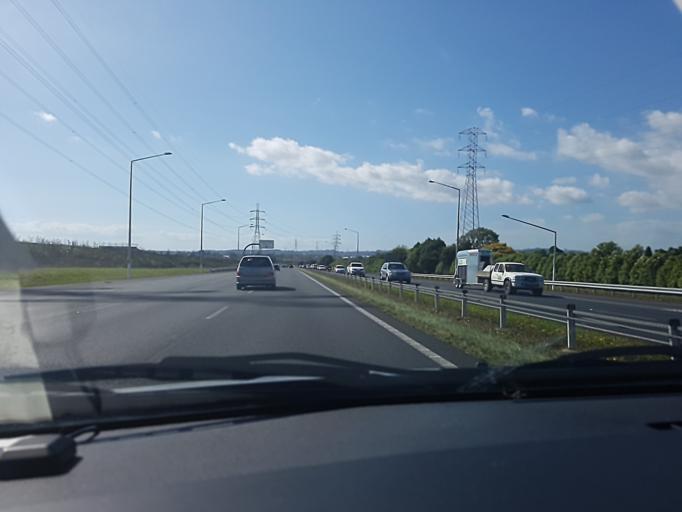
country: NZ
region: Auckland
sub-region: Auckland
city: Papakura
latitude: -37.0679
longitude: 174.9267
